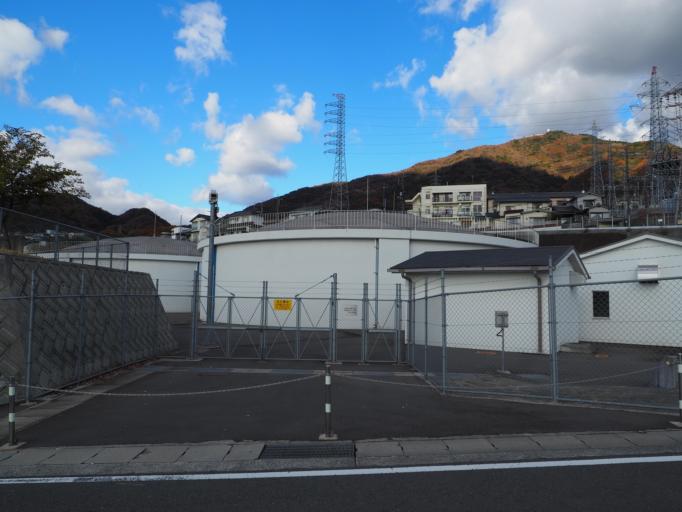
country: JP
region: Hiroshima
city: Kure
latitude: 34.2554
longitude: 132.5815
